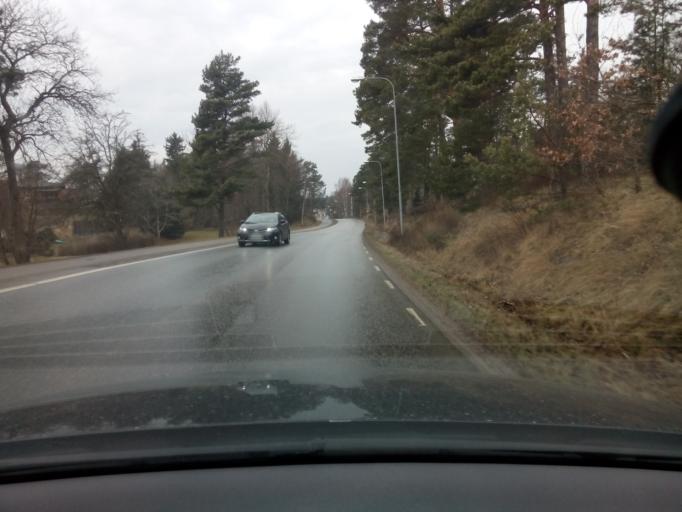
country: SE
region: Soedermanland
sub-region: Trosa Kommun
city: Trosa
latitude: 58.8987
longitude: 17.5367
